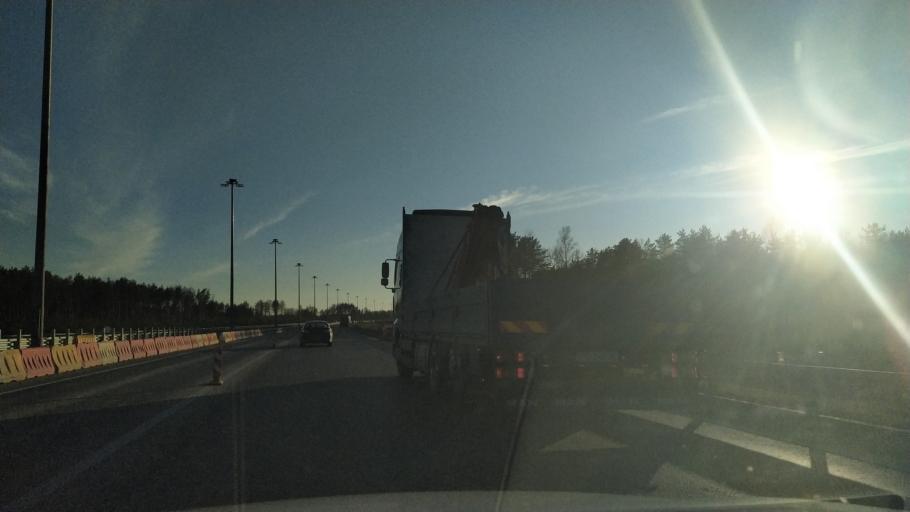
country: RU
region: St.-Petersburg
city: Levashovo
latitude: 60.0856
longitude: 30.2265
